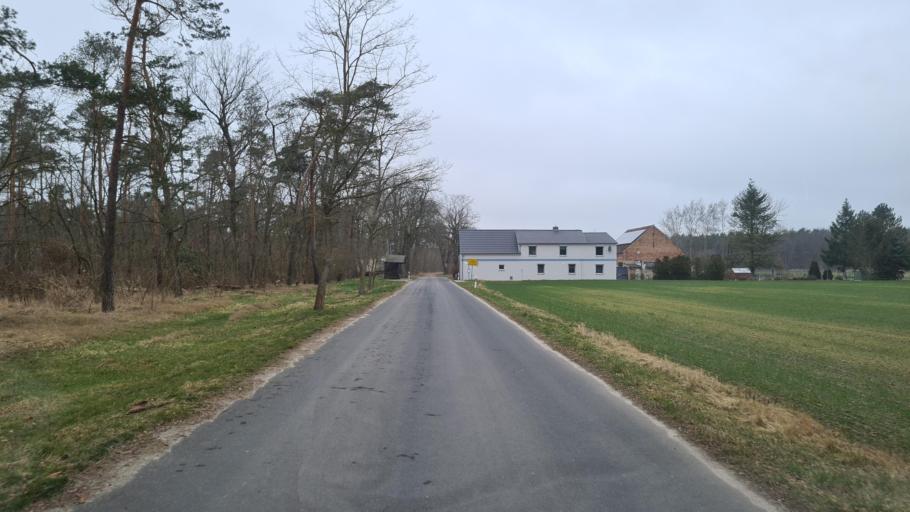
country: DE
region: Brandenburg
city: Herzberg
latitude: 51.6816
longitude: 13.1883
